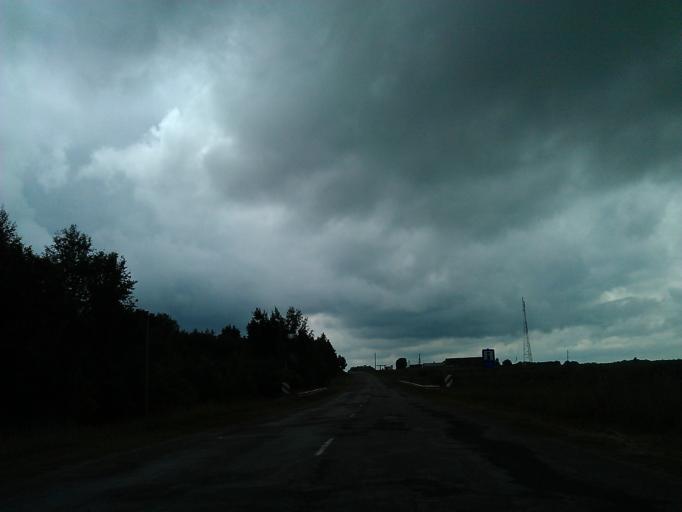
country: LV
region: Aizpute
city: Aizpute
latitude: 56.8428
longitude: 21.7718
